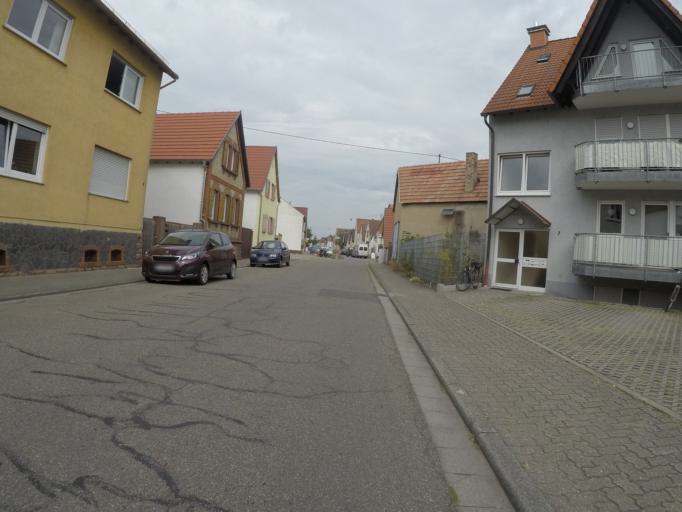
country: DE
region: Rheinland-Pfalz
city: Bohl-Iggelheim
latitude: 49.3595
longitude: 8.3136
